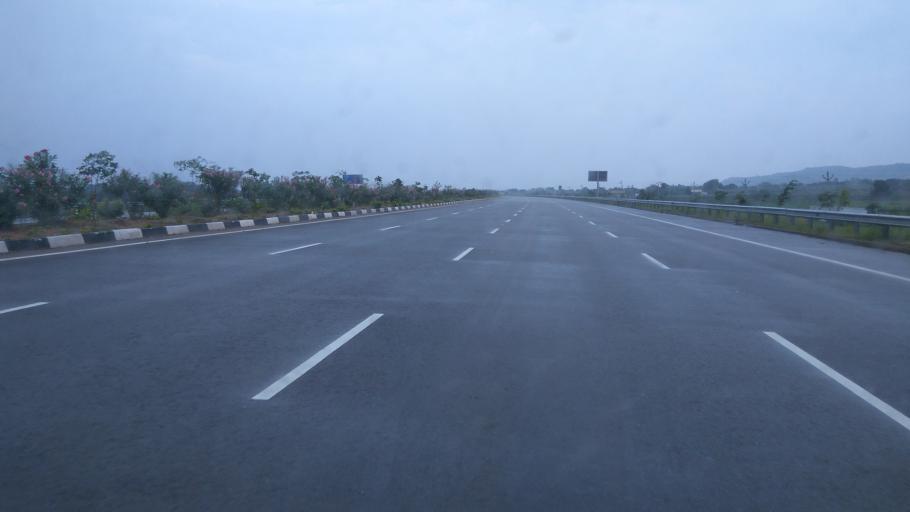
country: IN
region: Telangana
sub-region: Rangareddi
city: Ghatkesar
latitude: 17.4691
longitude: 78.6706
